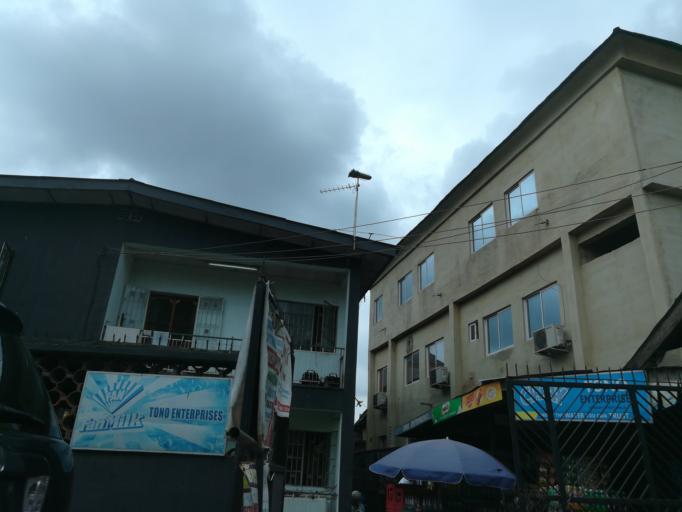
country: NG
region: Lagos
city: Ikeja
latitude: 6.5993
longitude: 3.3439
